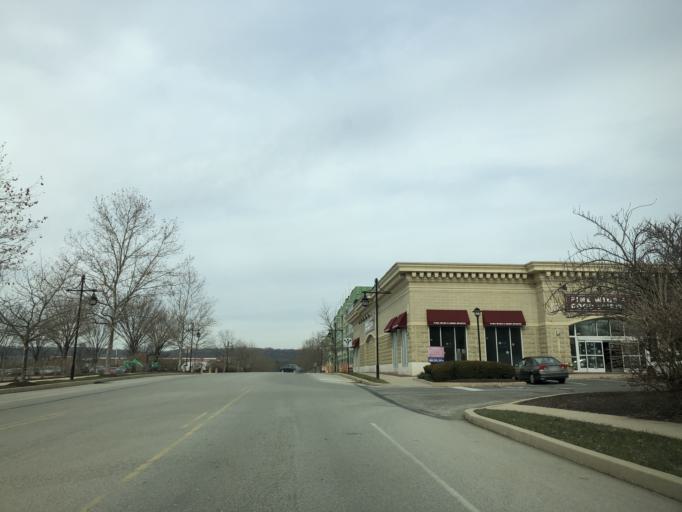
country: US
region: Pennsylvania
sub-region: Chester County
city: Exton
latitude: 40.0219
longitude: -75.6302
